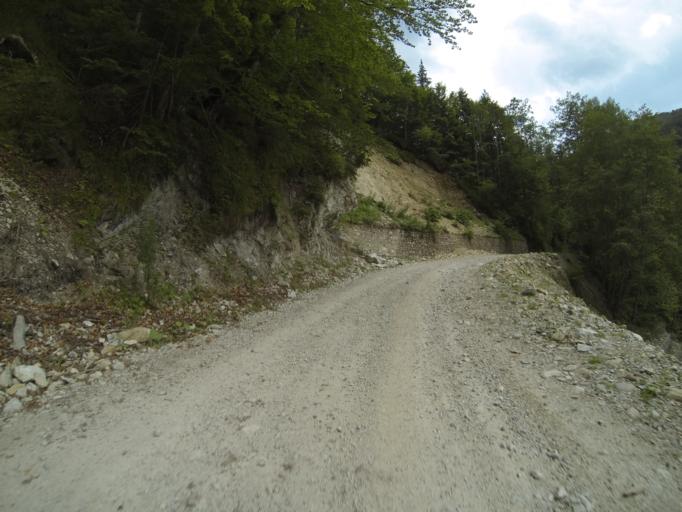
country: RO
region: Gorj
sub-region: Comuna Polovragi
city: Polovragi
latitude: 45.2295
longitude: 23.7716
